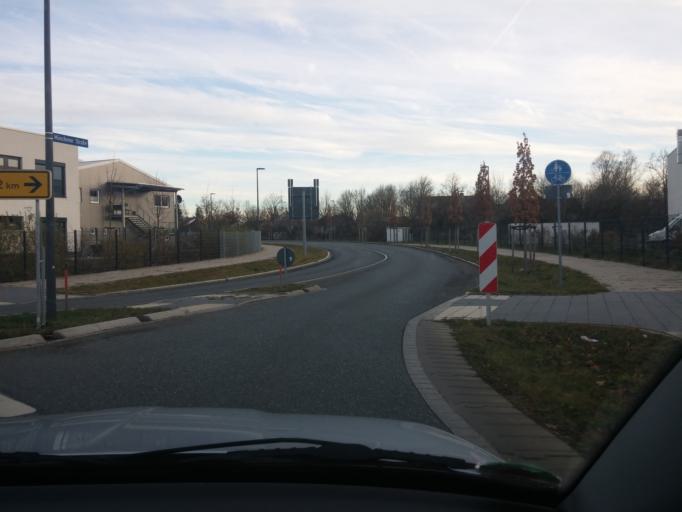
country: DE
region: Bavaria
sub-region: Upper Bavaria
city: Poing
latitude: 48.1448
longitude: 11.7891
